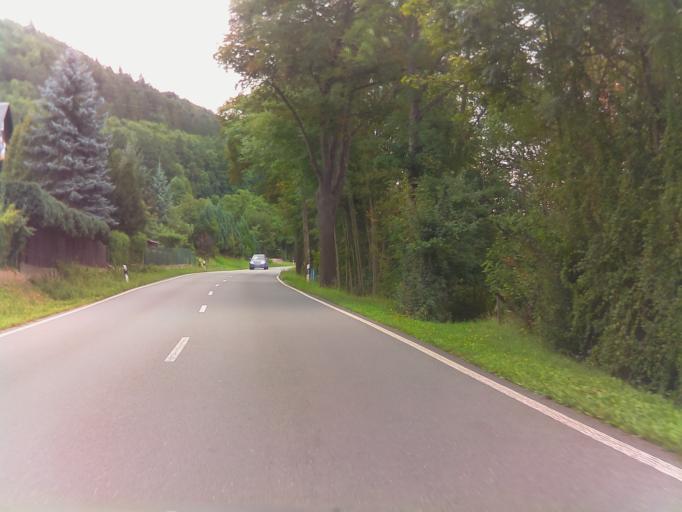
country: DE
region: Thuringia
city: Saalfeld
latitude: 50.6254
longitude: 11.3827
